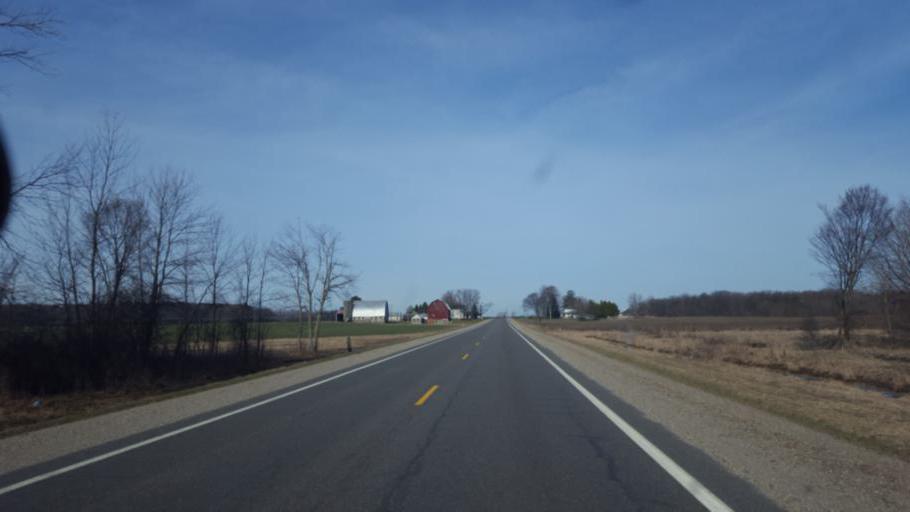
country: US
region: Michigan
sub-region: Montcalm County
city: Lakeview
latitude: 43.4327
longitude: -85.3565
